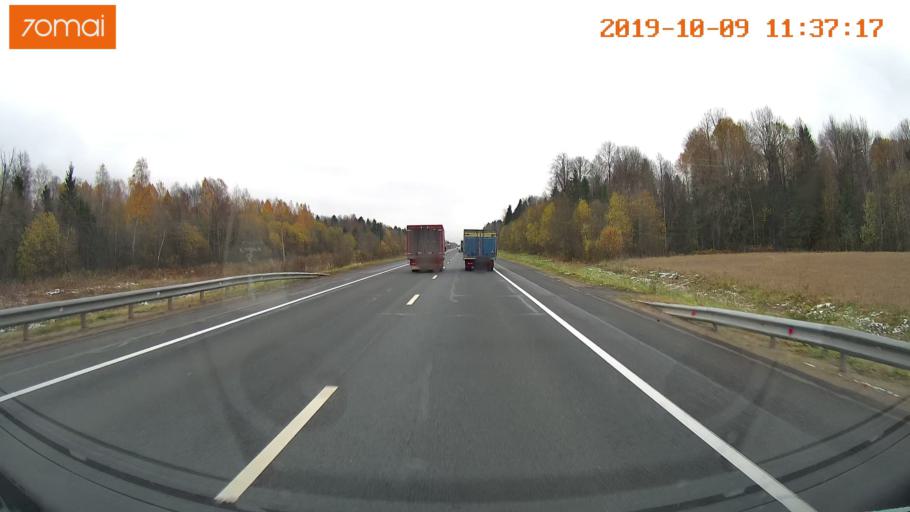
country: RU
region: Vologda
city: Gryazovets
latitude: 58.9811
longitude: 40.1448
